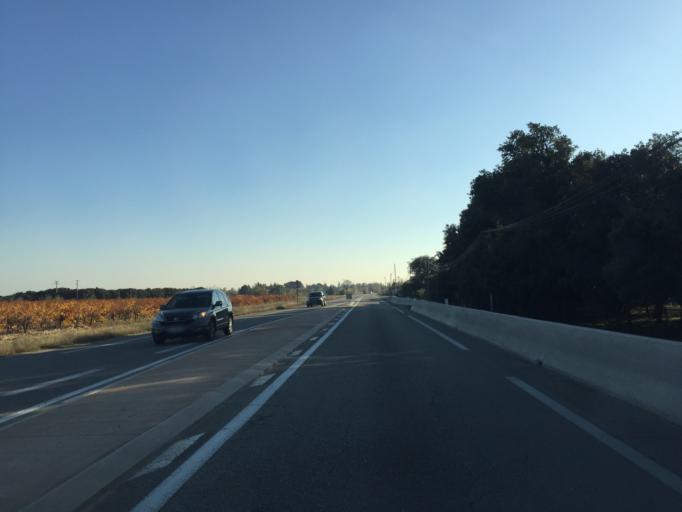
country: FR
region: Provence-Alpes-Cote d'Azur
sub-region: Departement du Vaucluse
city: Serignan-du-Comtat
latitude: 44.1819
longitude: 4.8551
